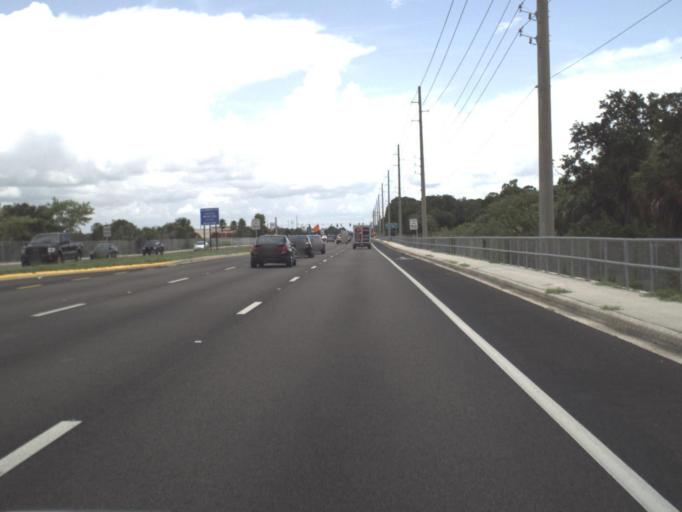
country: US
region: Florida
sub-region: Hillsborough County
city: Westchase
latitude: 28.0179
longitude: -82.6201
